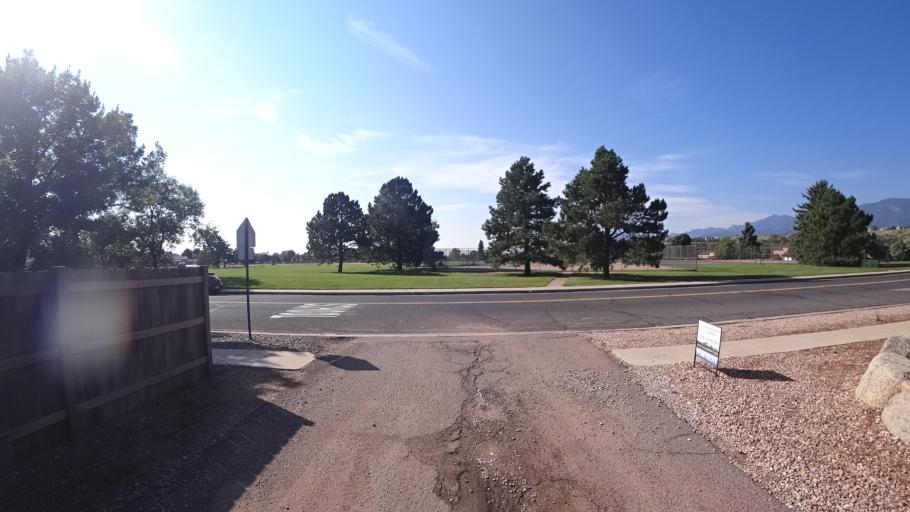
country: US
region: Colorado
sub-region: El Paso County
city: Colorado Springs
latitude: 38.8934
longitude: -104.8420
